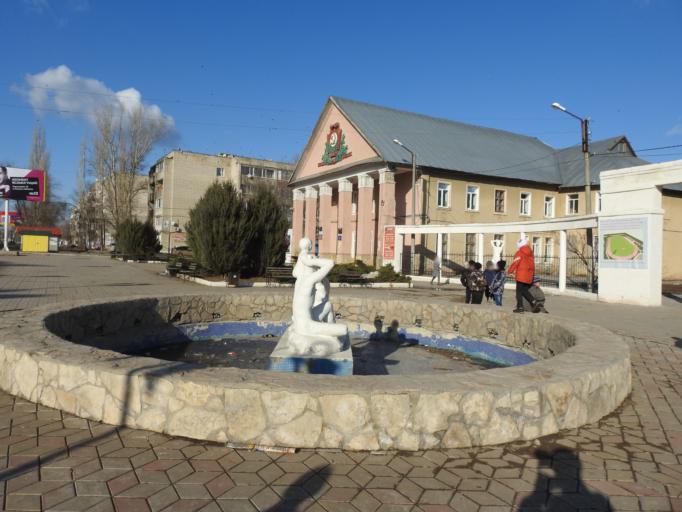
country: RU
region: Saratov
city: Yershov
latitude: 51.3518
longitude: 48.2836
